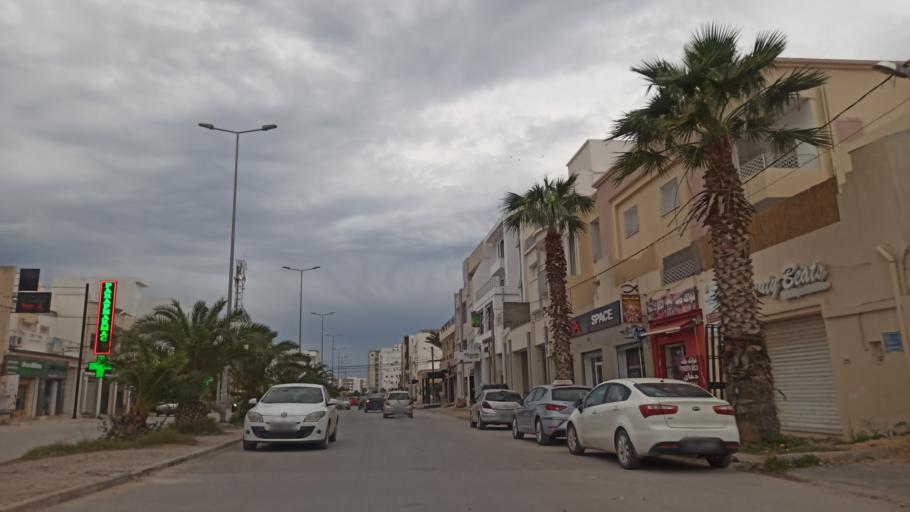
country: TN
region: Tunis
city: La Goulette
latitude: 36.8599
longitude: 10.2596
